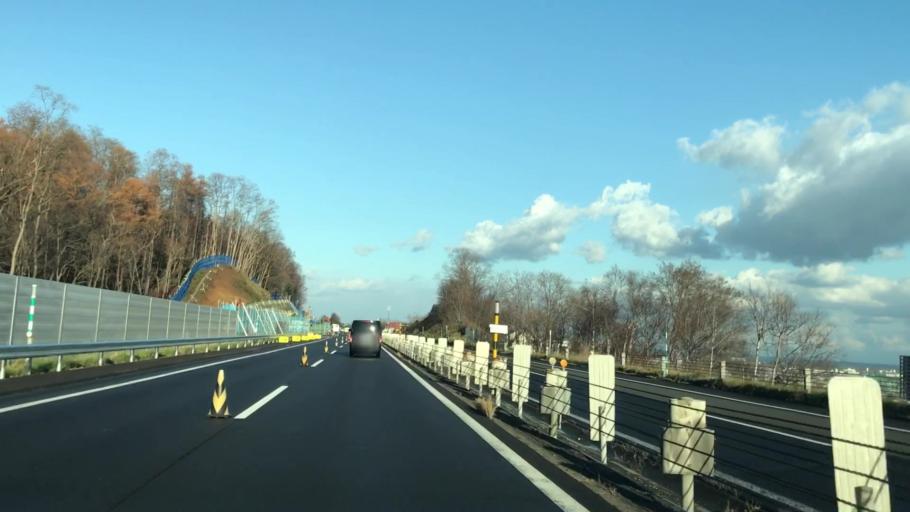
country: JP
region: Hokkaido
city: Sapporo
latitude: 43.1118
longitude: 141.2386
